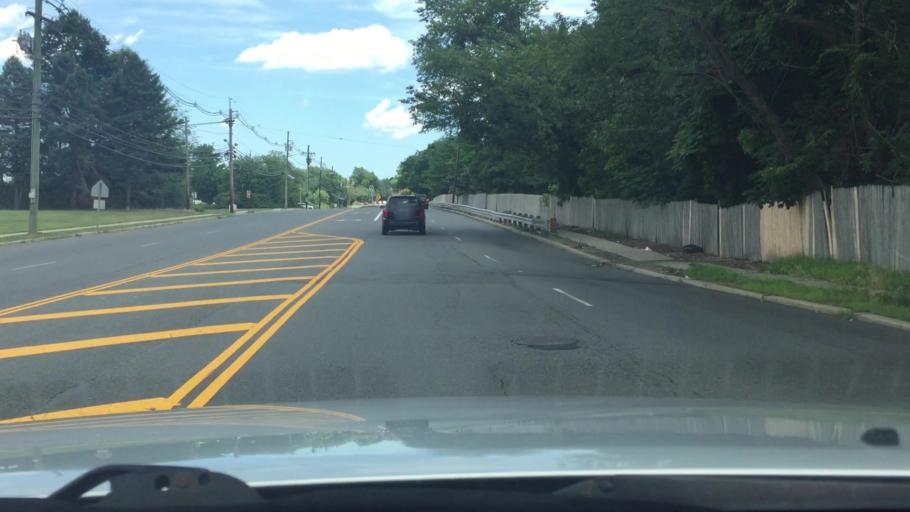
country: US
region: New Jersey
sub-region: Middlesex County
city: Old Bridge
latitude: 40.4202
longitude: -74.3828
